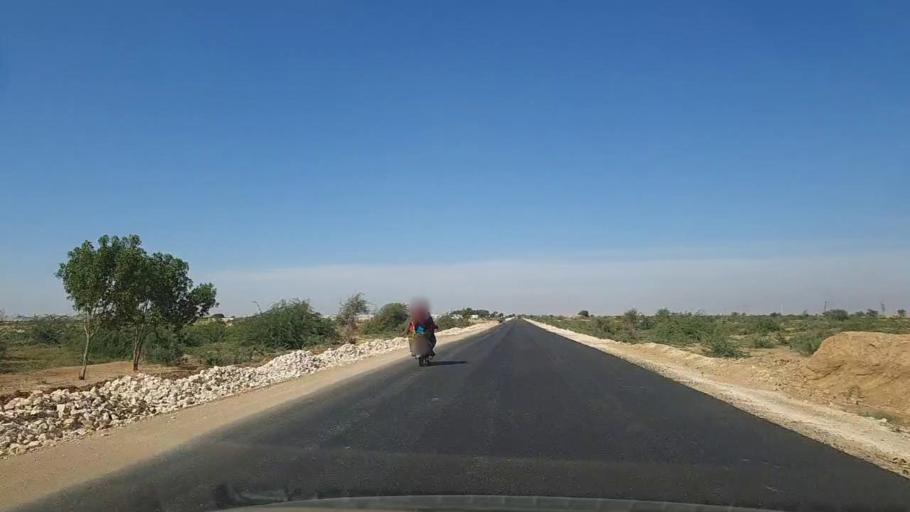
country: PK
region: Sindh
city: Kotri
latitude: 25.2521
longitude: 68.2270
